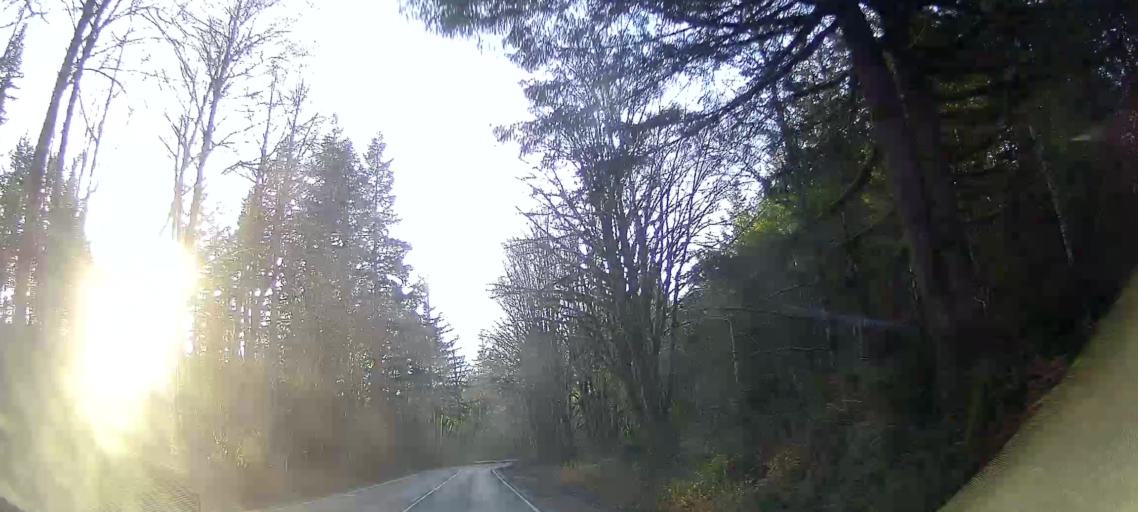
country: US
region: Washington
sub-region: Skagit County
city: Sedro-Woolley
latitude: 48.5543
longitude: -121.8533
